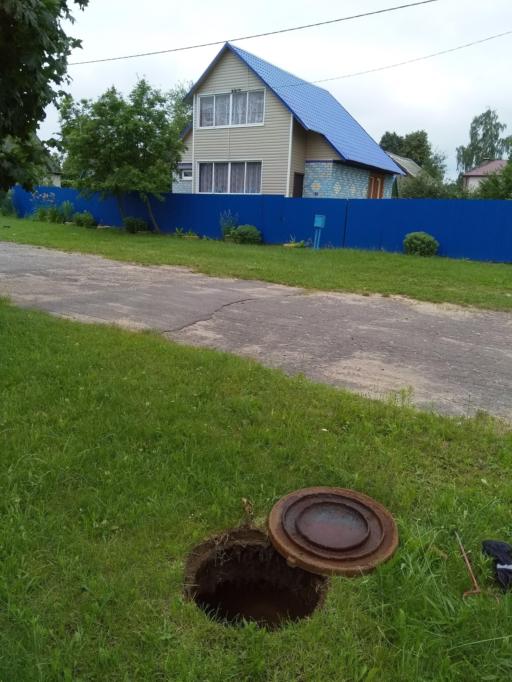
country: BY
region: Mogilev
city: Myazhysyatki
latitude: 53.7804
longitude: 30.0119
